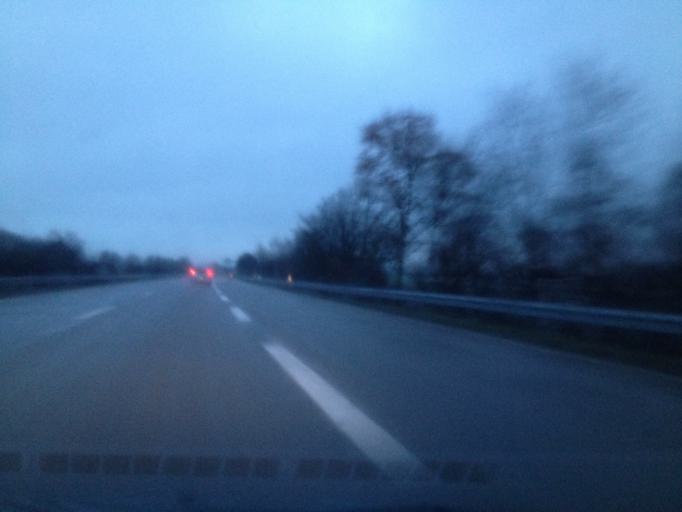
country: DE
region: Rheinland-Pfalz
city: Kruft
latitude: 50.3940
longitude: 7.3160
